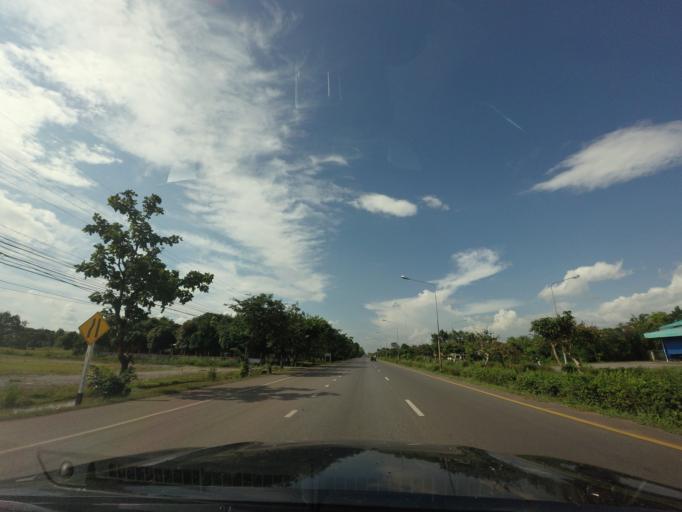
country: TH
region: Nong Khai
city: Sa Khrai
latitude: 17.6920
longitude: 102.7825
